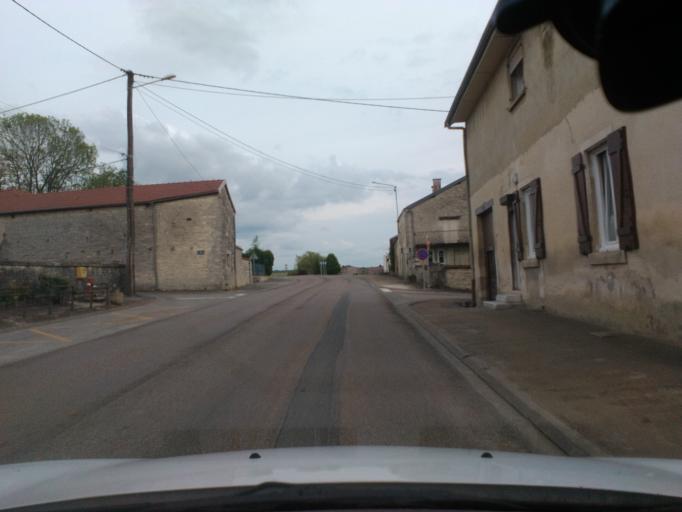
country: FR
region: Champagne-Ardenne
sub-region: Departement de la Haute-Marne
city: Lavilleneuve-au-Roi
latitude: 48.1731
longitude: 4.9960
